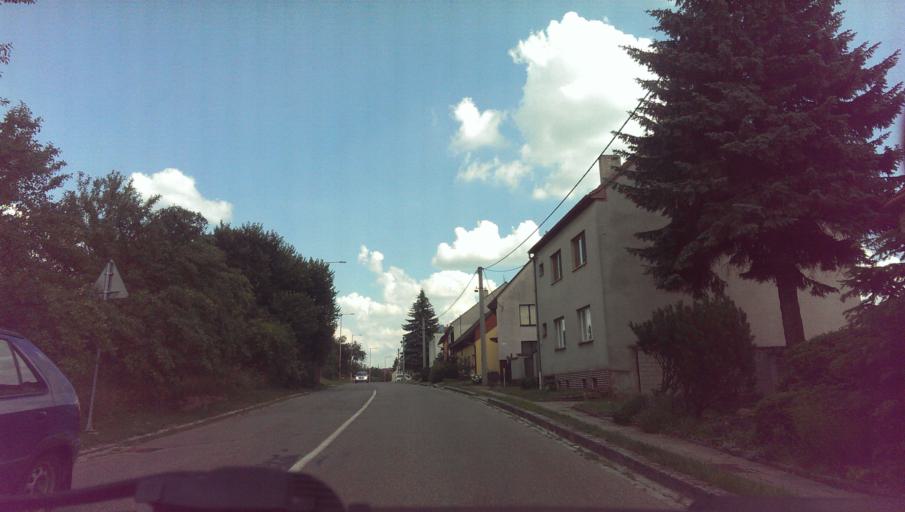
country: CZ
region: Zlin
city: Kunovice
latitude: 49.0472
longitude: 17.4975
